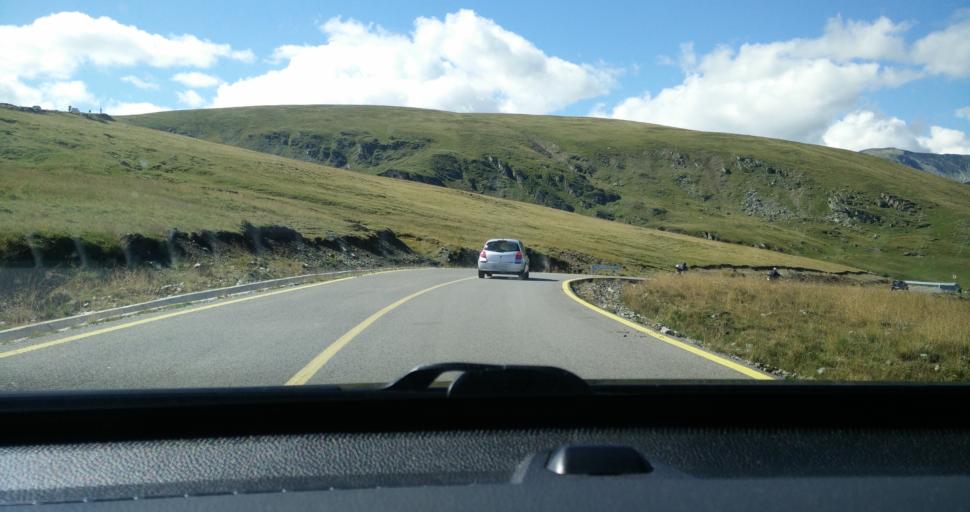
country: RO
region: Gorj
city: Novaci-Straini
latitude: 45.3797
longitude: 23.6511
